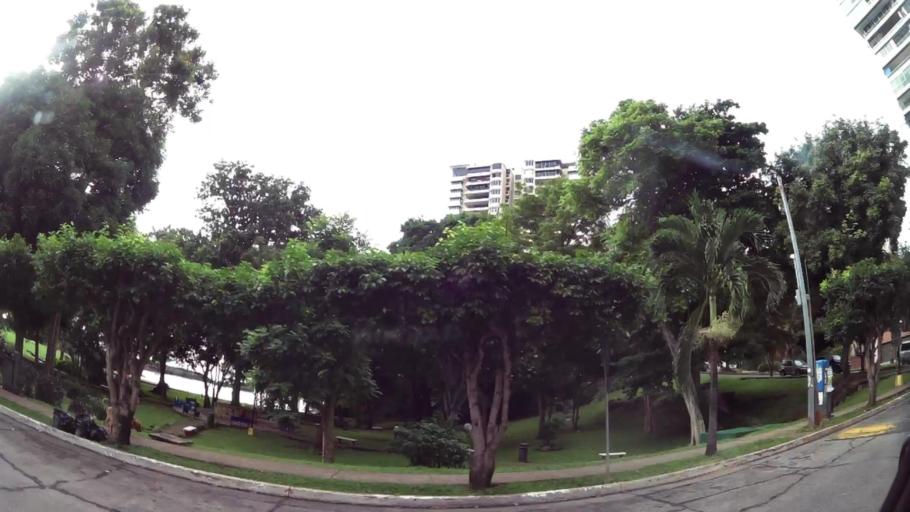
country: PA
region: Panama
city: Panama
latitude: 8.9759
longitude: -79.5124
